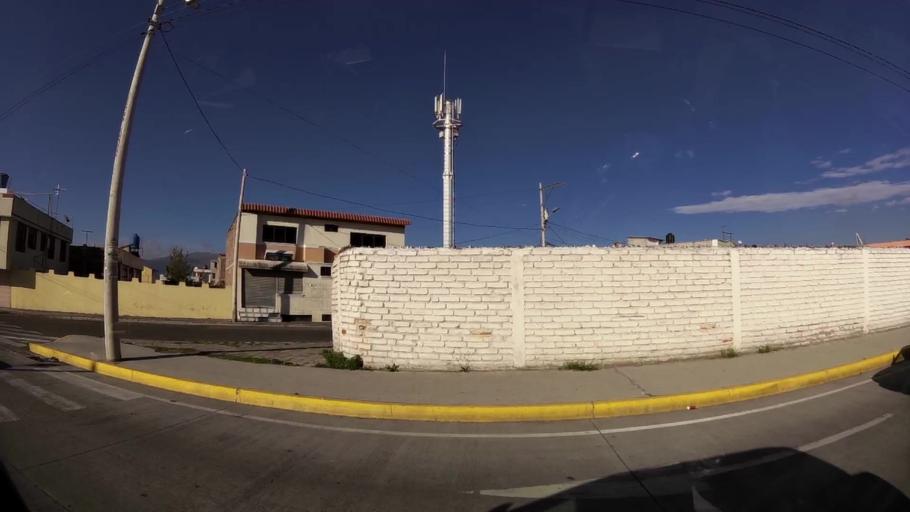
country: EC
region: Chimborazo
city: Riobamba
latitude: -1.6688
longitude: -78.6379
